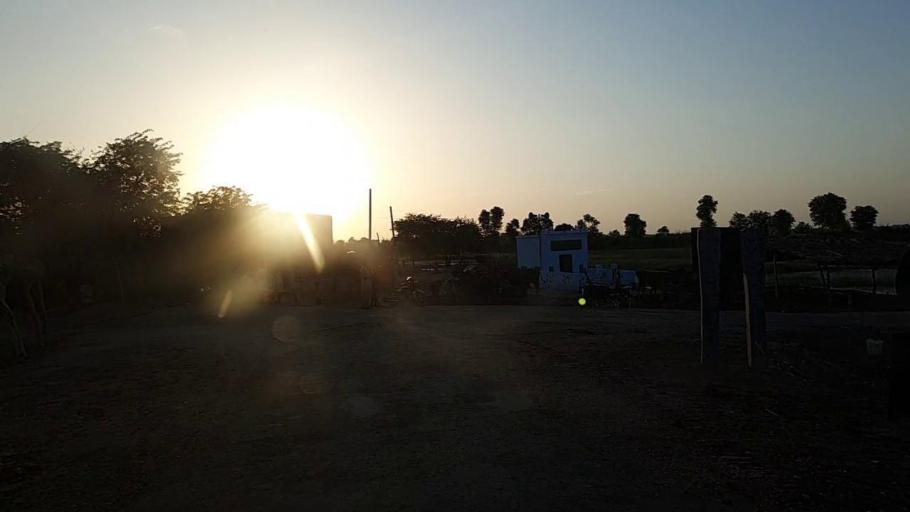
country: PK
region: Sindh
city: Hingorja
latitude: 27.0613
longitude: 68.3944
